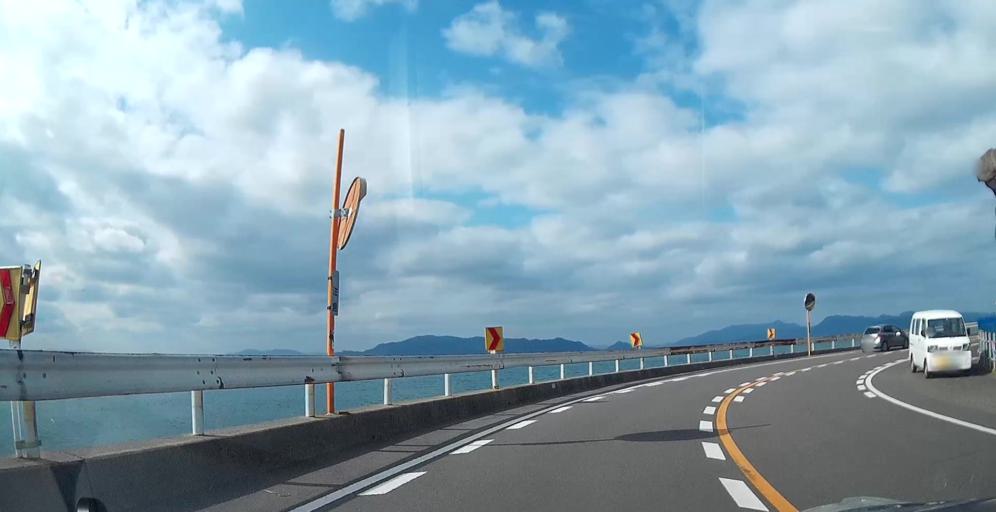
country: JP
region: Kumamoto
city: Minamata
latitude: 32.3118
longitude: 130.4694
